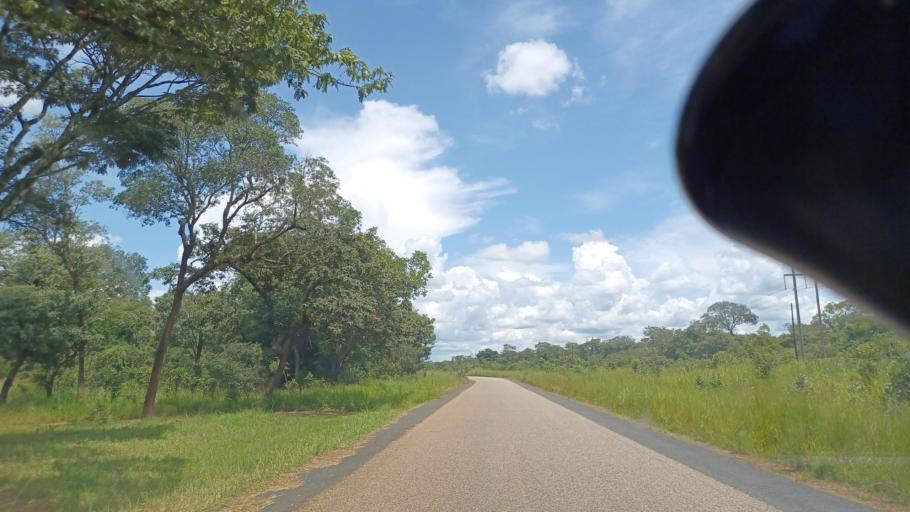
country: ZM
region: North-Western
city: Solwezi
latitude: -12.5782
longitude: 26.1316
